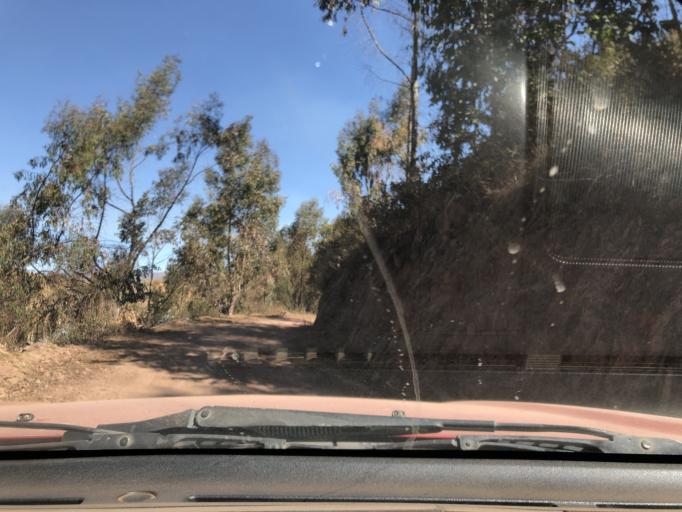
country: PE
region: Ayacucho
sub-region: Provincia de La Mar
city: Chilcas
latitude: -13.1841
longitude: -73.8420
